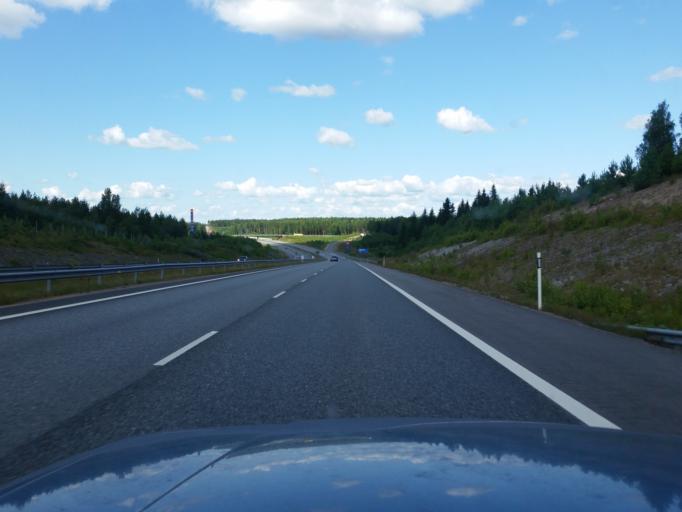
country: FI
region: Varsinais-Suomi
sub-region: Salo
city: Suomusjaervi
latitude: 60.3772
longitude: 23.6347
